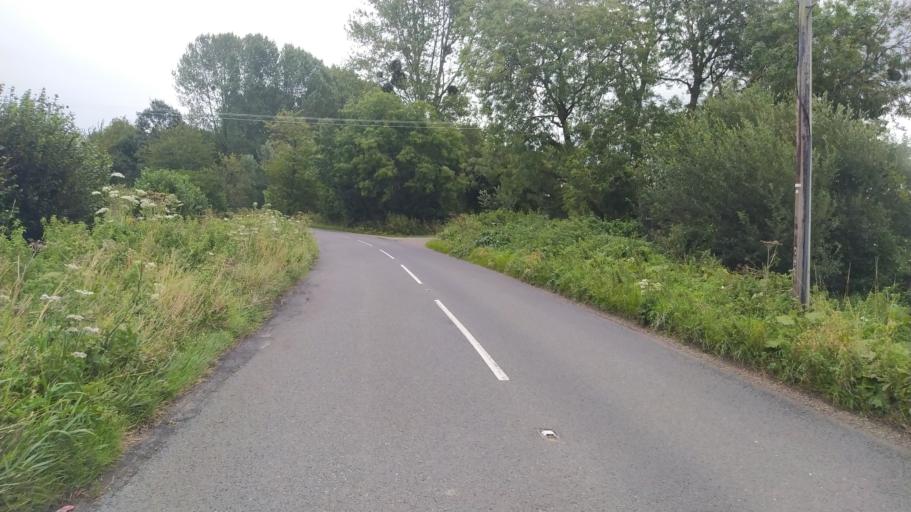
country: GB
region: England
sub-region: Dorset
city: Verwood
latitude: 50.9163
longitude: -1.9135
